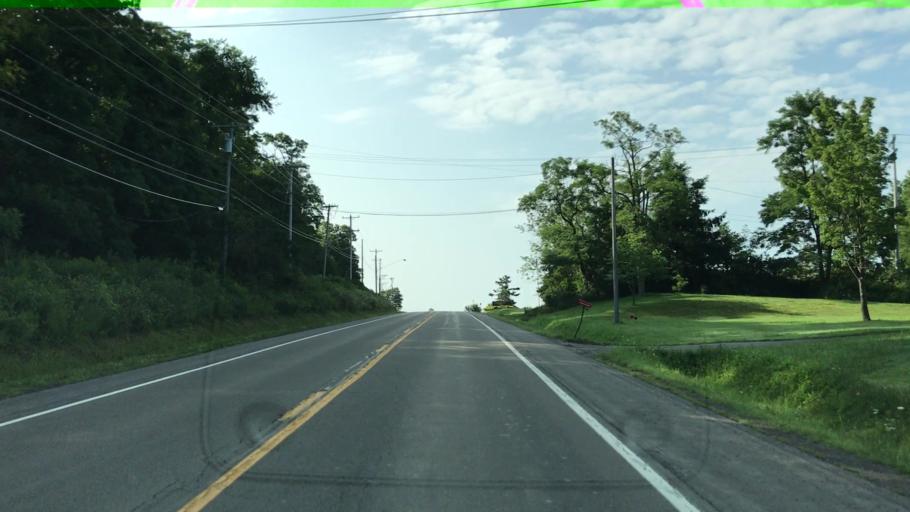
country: US
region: New York
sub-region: Chautauqua County
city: Mayville
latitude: 42.2489
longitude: -79.4633
